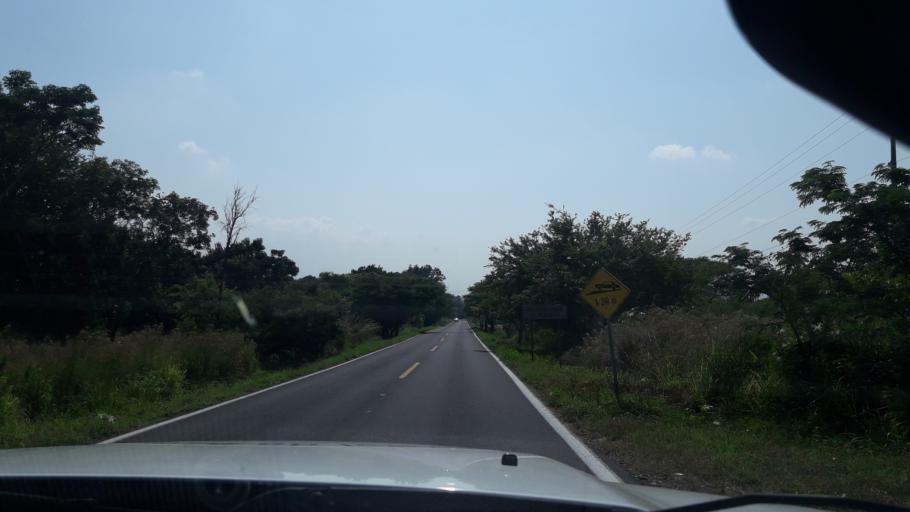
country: MX
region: Colima
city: Comala
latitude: 19.3359
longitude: -103.7465
